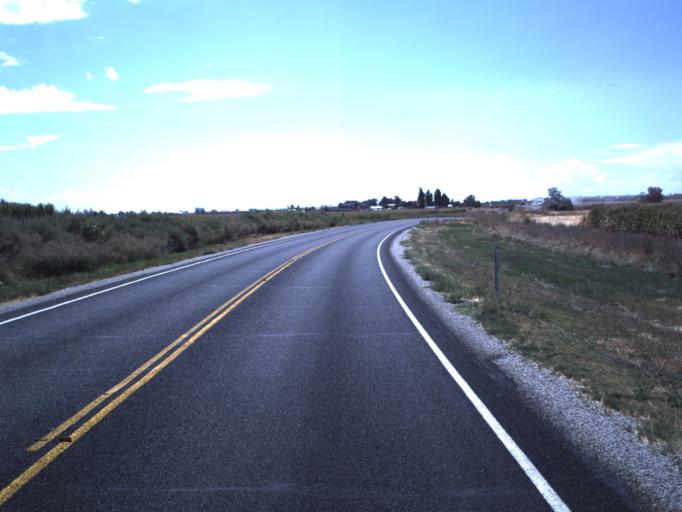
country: US
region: Utah
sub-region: Box Elder County
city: Honeyville
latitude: 41.5977
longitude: -112.1275
